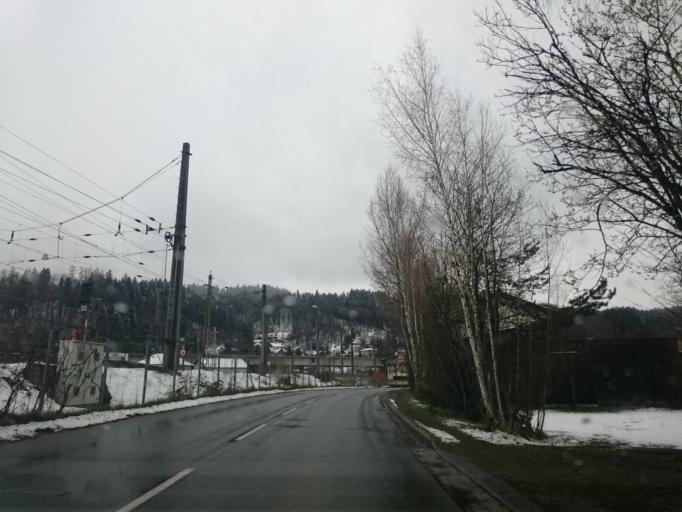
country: AT
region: Tyrol
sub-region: Politischer Bezirk Kufstein
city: Kufstein
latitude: 47.5870
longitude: 12.1657
